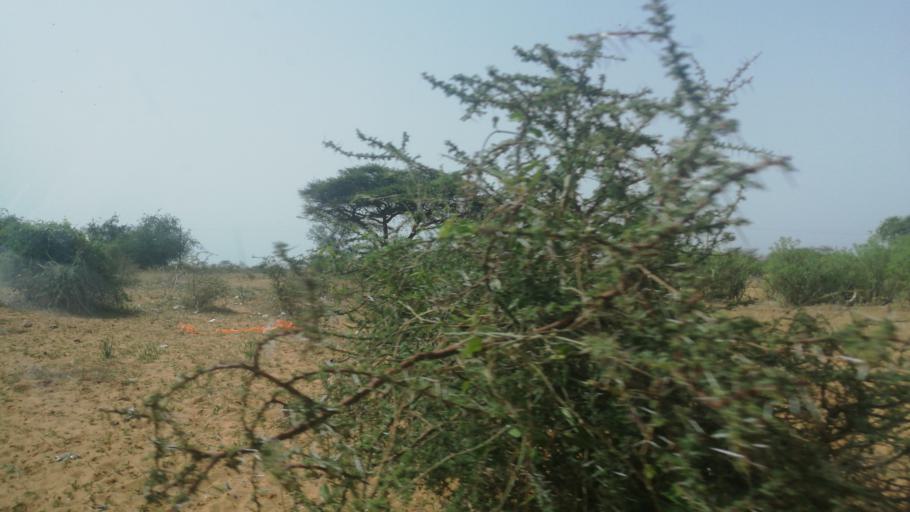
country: SN
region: Saint-Louis
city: Saint-Louis
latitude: 16.0539
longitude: -16.3338
